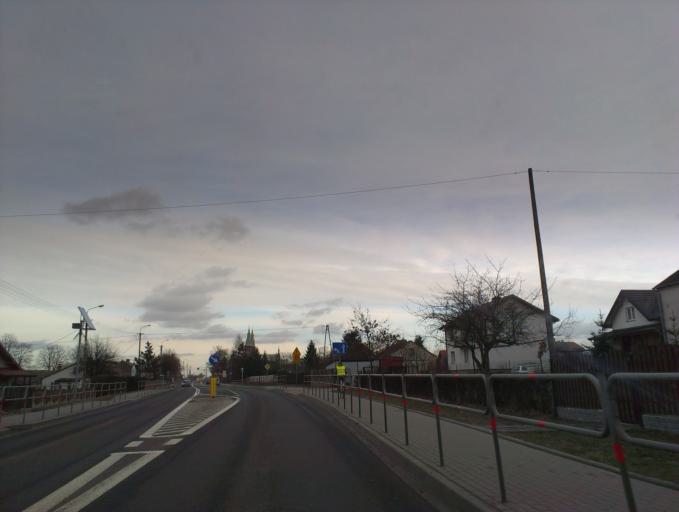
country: PL
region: Masovian Voivodeship
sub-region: Powiat sierpecki
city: Szczutowo
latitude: 52.9017
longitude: 19.5204
